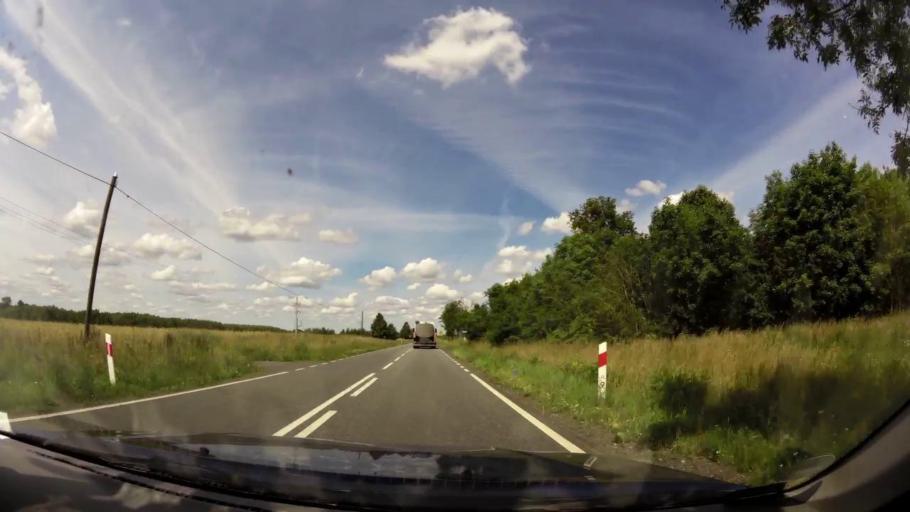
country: PL
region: West Pomeranian Voivodeship
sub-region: Powiat lobeski
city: Wegorzyno
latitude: 53.5227
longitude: 15.5676
